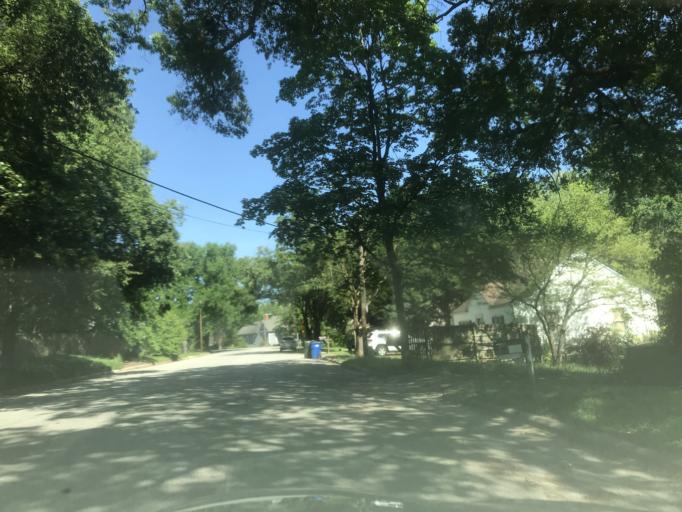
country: US
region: North Carolina
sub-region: Wake County
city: Raleigh
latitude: 35.7608
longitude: -78.6463
